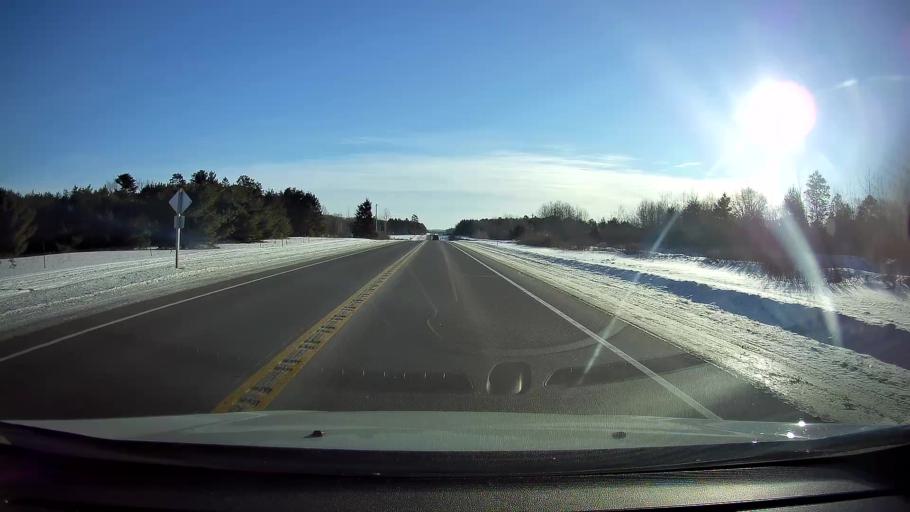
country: US
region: Wisconsin
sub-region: Sawyer County
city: Hayward
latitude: 45.9855
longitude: -91.5838
